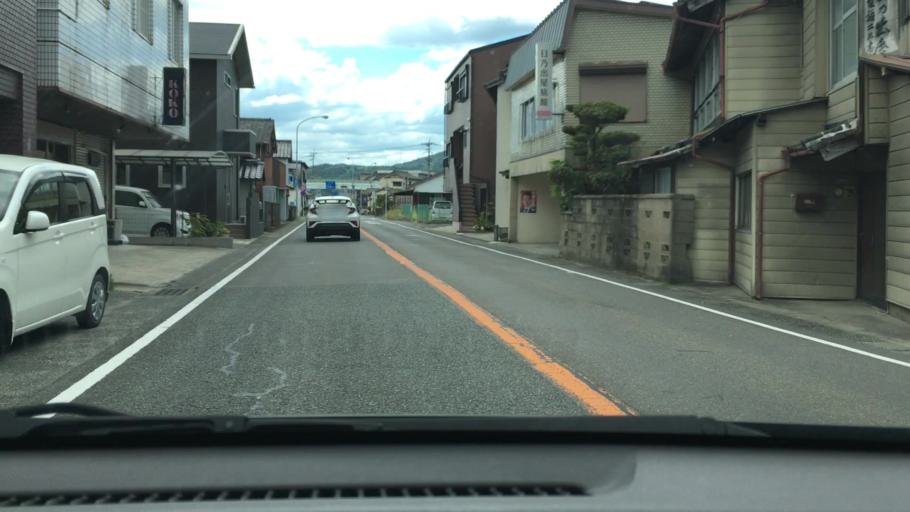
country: JP
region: Saga Prefecture
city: Kashima
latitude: 33.2198
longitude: 130.1603
